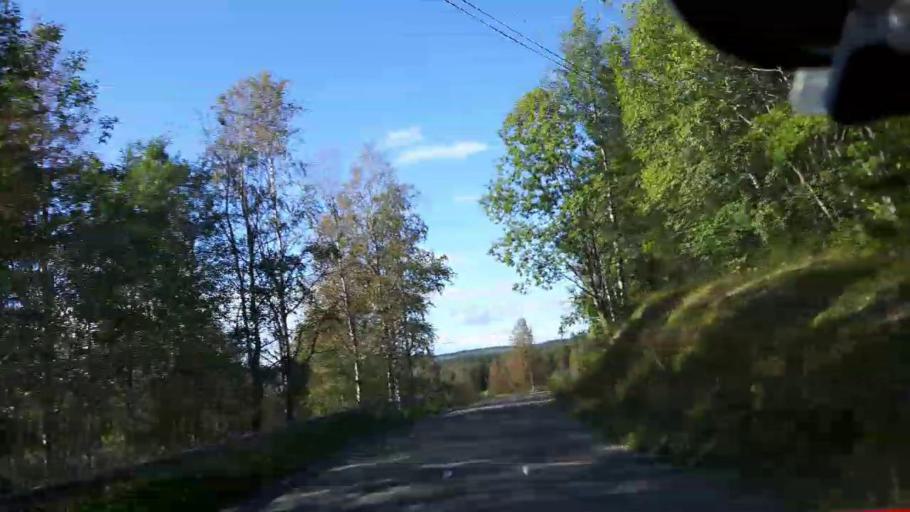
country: SE
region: Jaemtland
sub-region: Ragunda Kommun
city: Hammarstrand
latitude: 63.4941
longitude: 16.0389
